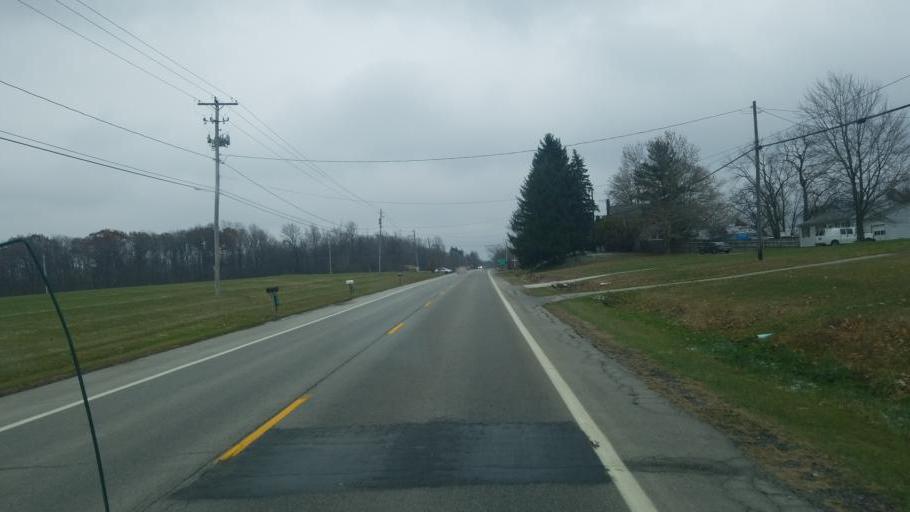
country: US
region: Ohio
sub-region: Medina County
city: Medina
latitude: 41.1533
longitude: -81.9021
